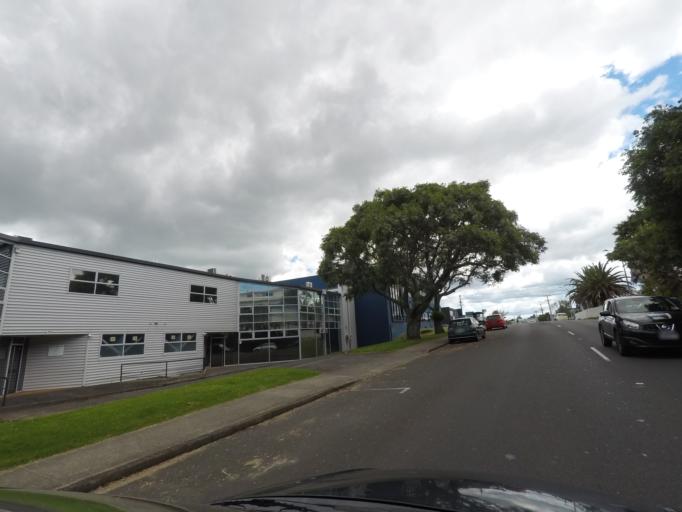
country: NZ
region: Auckland
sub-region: Auckland
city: Auckland
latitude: -36.8786
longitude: 174.7350
